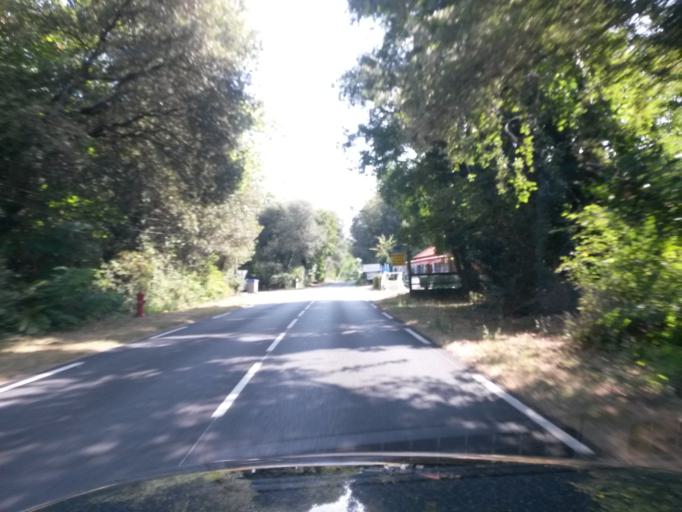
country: FR
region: Pays de la Loire
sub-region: Departement de la Vendee
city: Olonne-sur-Mer
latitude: 46.5777
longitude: -1.8229
